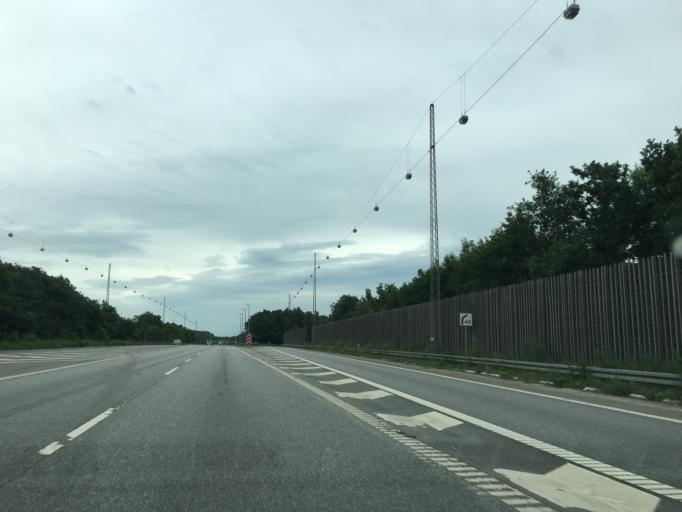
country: DK
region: Capital Region
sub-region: Hoje-Taastrup Kommune
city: Taastrup
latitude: 55.6604
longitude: 12.3132
